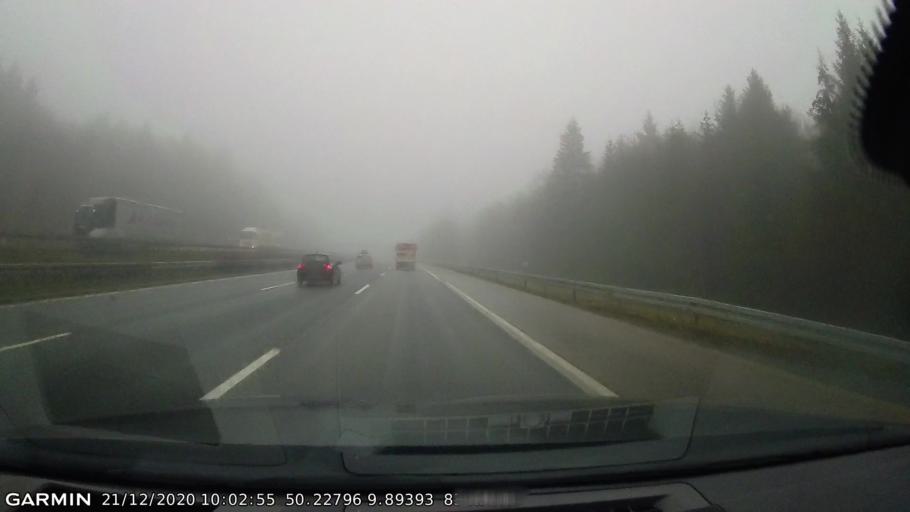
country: DE
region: Bavaria
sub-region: Regierungsbezirk Unterfranken
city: Schondra
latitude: 50.2282
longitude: 9.8937
